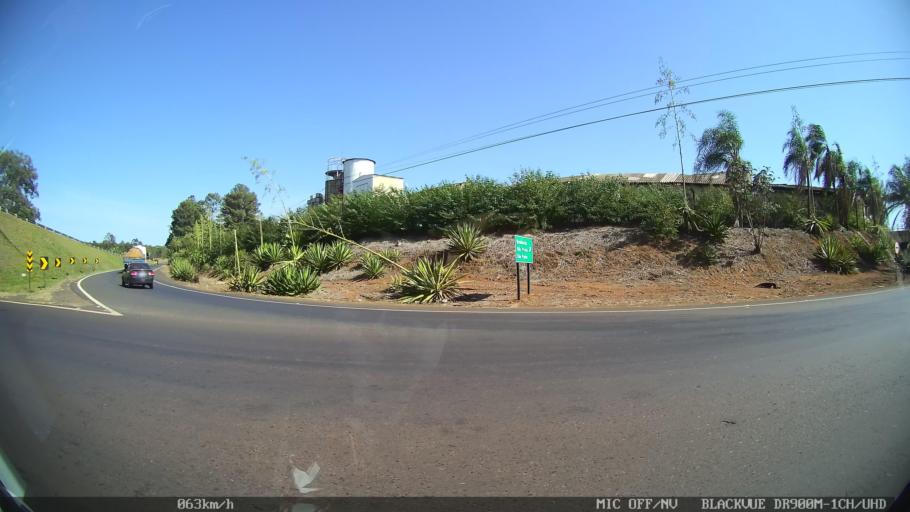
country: BR
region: Sao Paulo
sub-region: Batatais
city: Batatais
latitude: -20.9009
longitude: -47.6076
